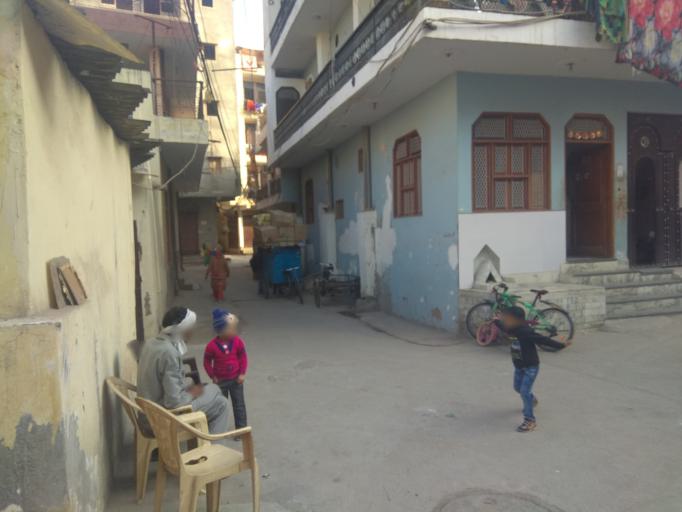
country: IN
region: NCT
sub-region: West Delhi
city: Nangloi Jat
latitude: 28.6375
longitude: 77.0688
